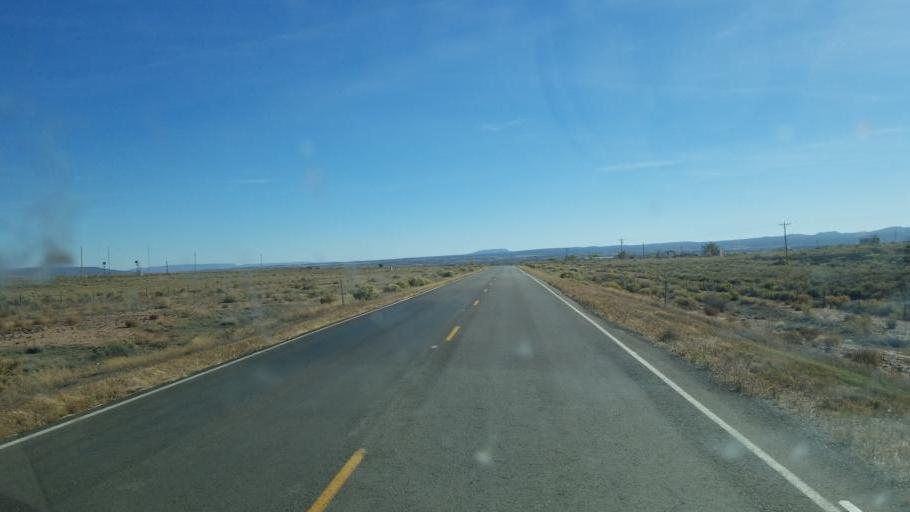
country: US
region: New Mexico
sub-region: Cibola County
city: Milan
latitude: 35.3025
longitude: -107.9877
